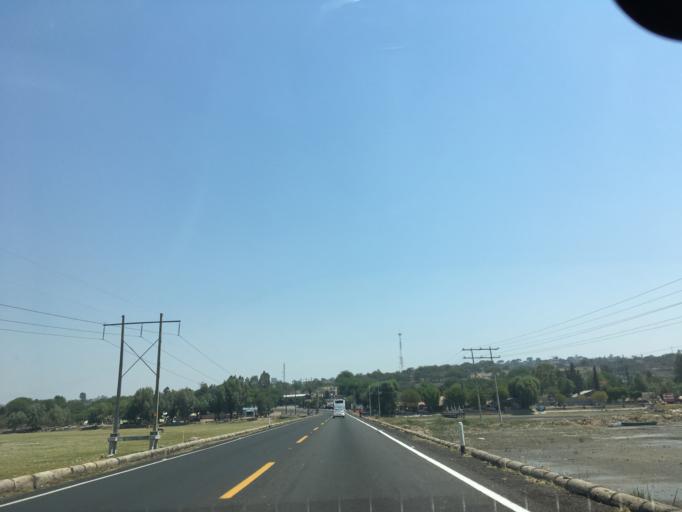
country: MX
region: Michoacan
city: Cuitzeo del Porvenir
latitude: 19.9561
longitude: -101.1360
